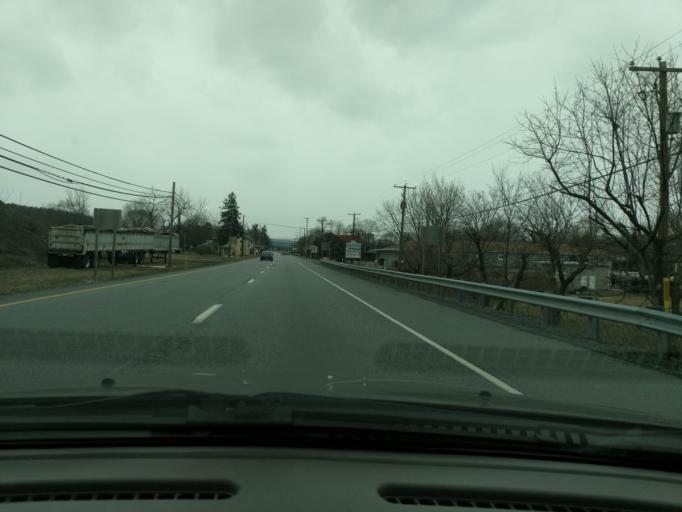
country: US
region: Pennsylvania
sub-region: Schuylkill County
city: Orwigsburg
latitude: 40.6238
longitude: -76.0602
